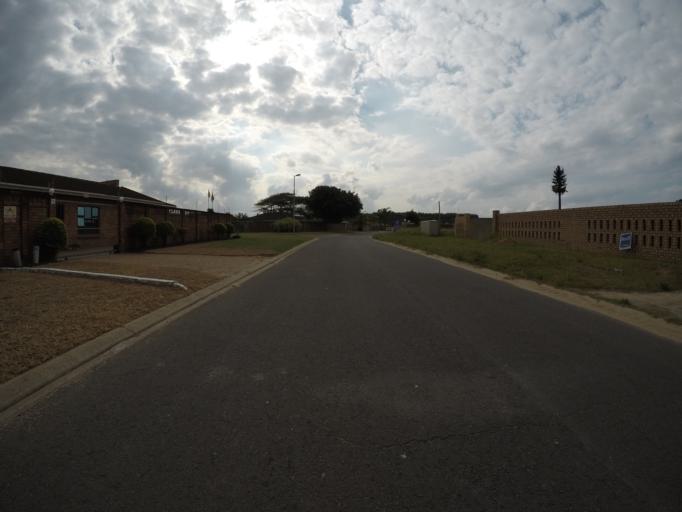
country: ZA
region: KwaZulu-Natal
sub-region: uThungulu District Municipality
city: Richards Bay
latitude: -28.7346
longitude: 32.0861
